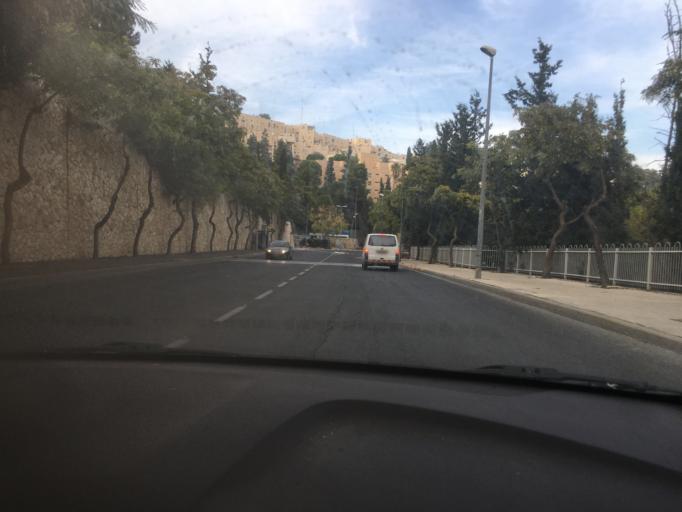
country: IL
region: Jerusalem
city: Jerusalem
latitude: 31.7483
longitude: 35.2330
